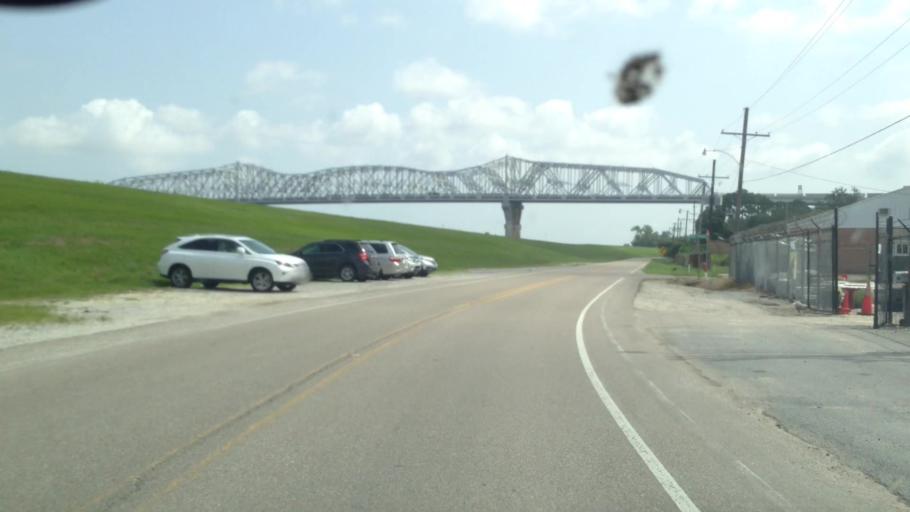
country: US
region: Louisiana
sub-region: Jefferson Parish
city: Bridge City
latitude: 29.9362
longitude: -90.1709
